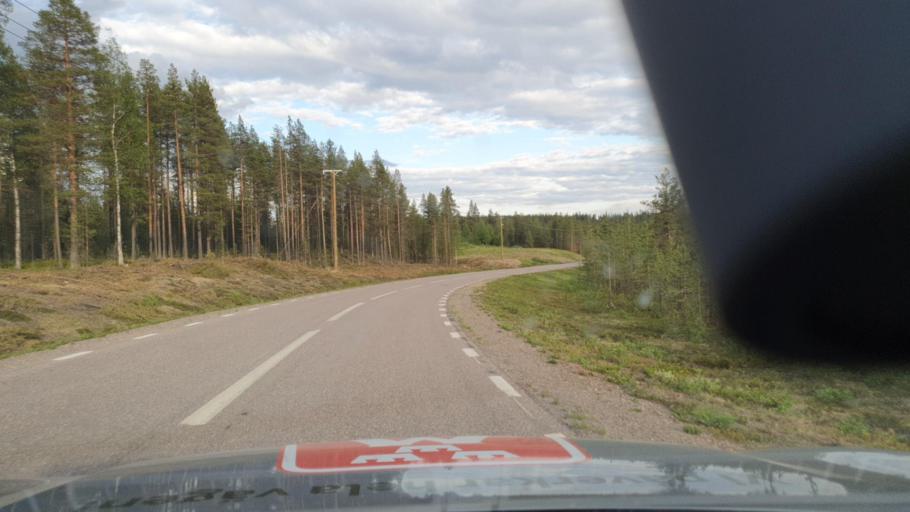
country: SE
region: Norrbotten
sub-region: Gallivare Kommun
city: Gaellivare
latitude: 66.9444
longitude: 21.2446
